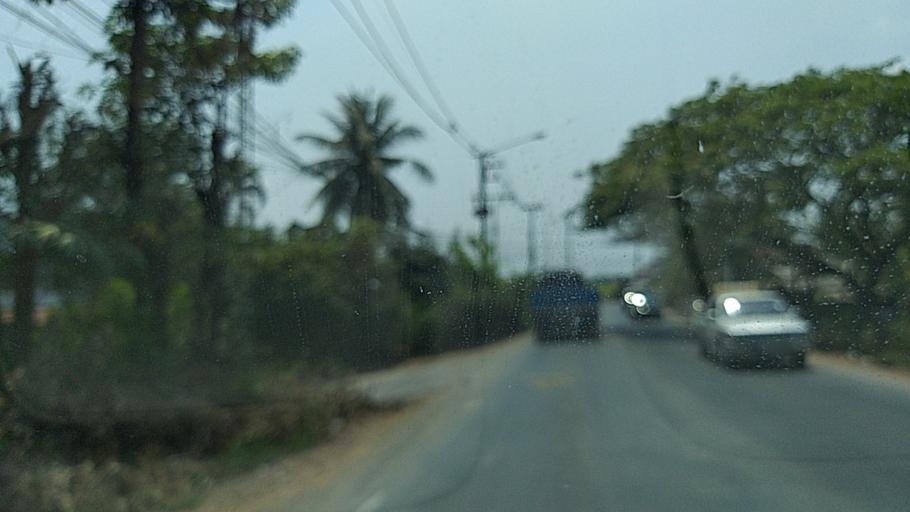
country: TH
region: Chachoengsao
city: Bang Nam Priao
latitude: 13.9680
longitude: 100.9663
